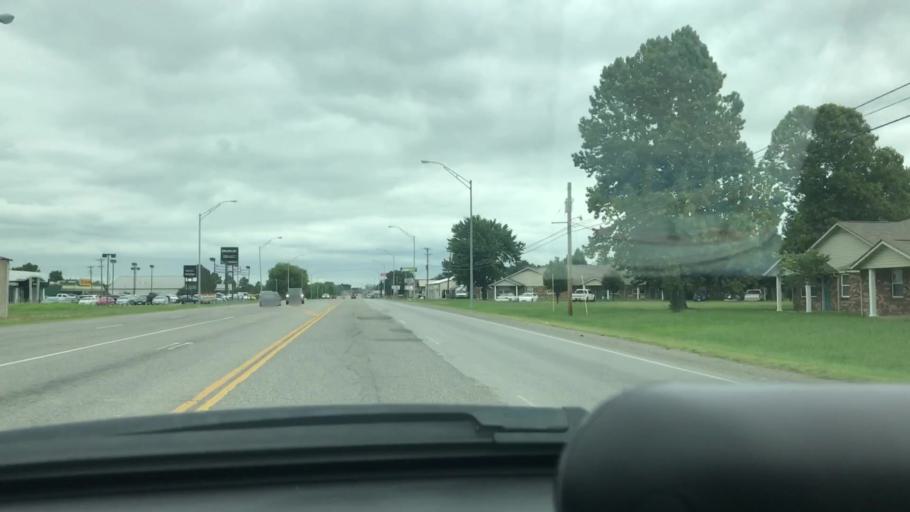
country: US
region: Oklahoma
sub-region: Wagoner County
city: Wagoner
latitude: 35.9446
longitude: -95.3952
